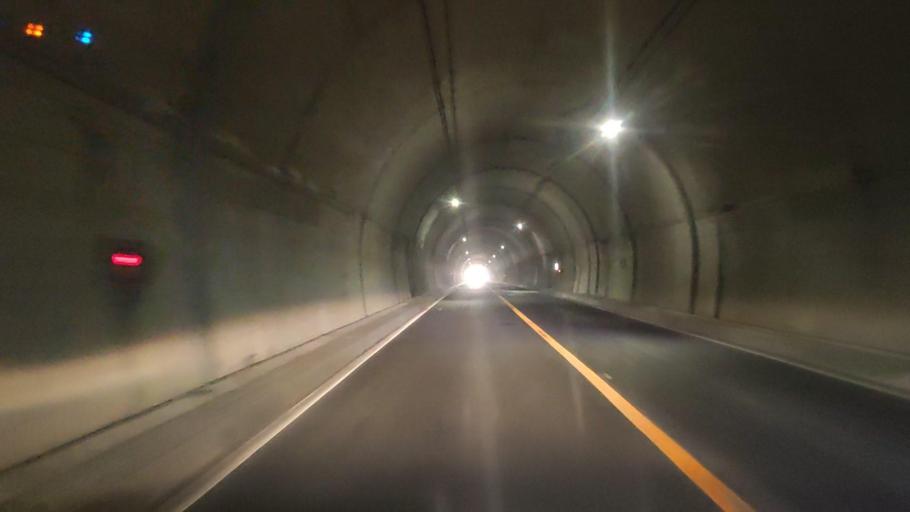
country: JP
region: Oita
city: Saiki
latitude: 32.8828
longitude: 131.9467
